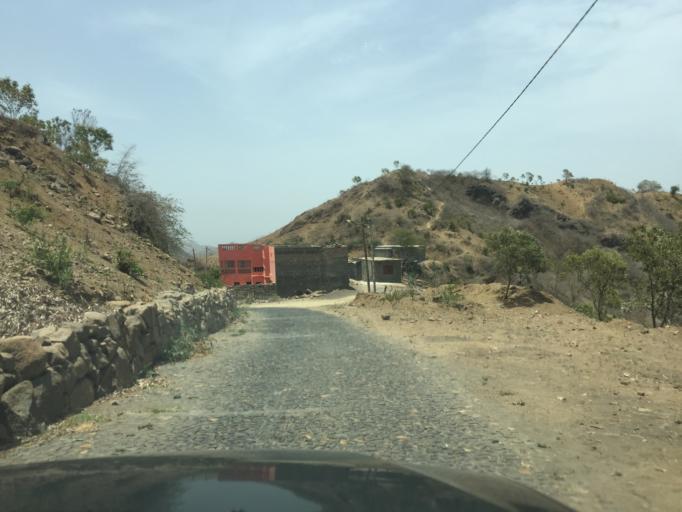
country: CV
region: Sao Salvador do Mundo
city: Picos
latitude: 15.0923
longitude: -23.6487
